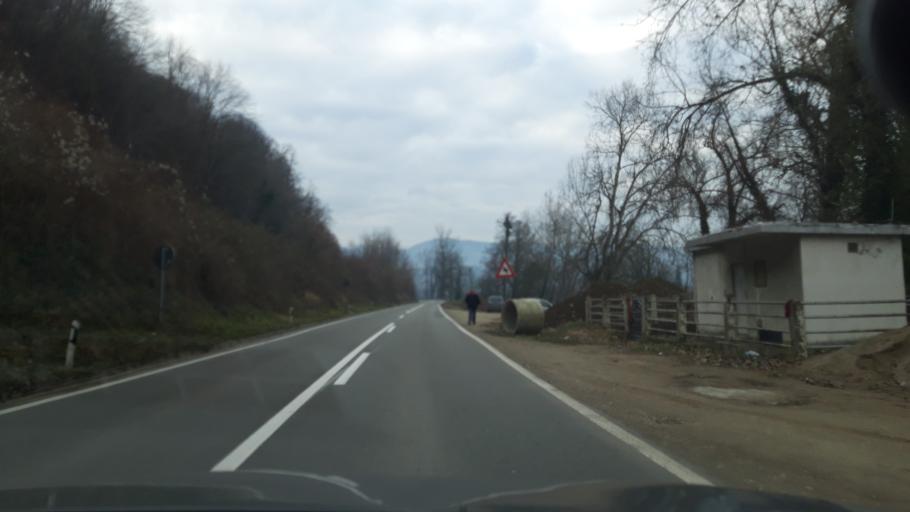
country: BA
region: Republika Srpska
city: Zvornik
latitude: 44.4196
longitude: 19.1486
